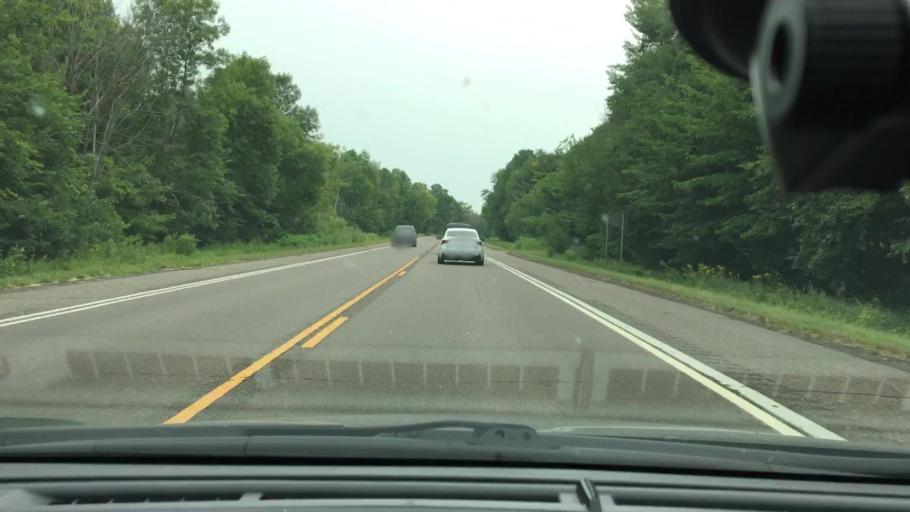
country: US
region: Minnesota
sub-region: Mille Lacs County
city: Vineland
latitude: 46.1295
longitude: -93.6831
